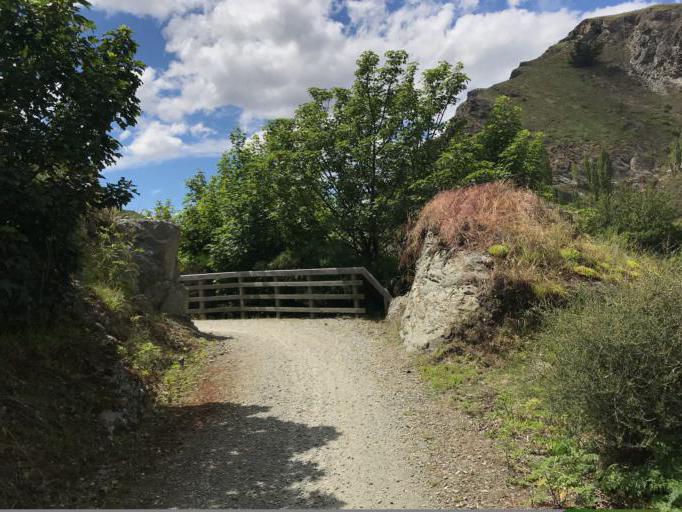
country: NZ
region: Otago
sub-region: Queenstown-Lakes District
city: Arrowtown
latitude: -45.0094
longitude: 168.8952
